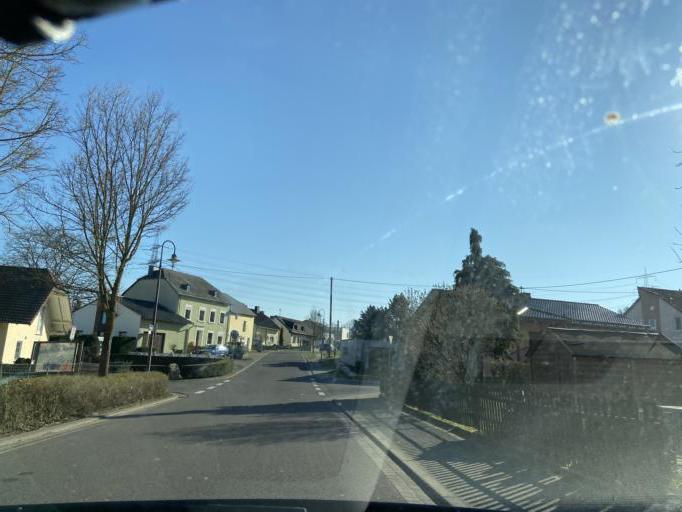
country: DE
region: Rheinland-Pfalz
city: Aach
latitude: 49.8021
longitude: 6.6056
